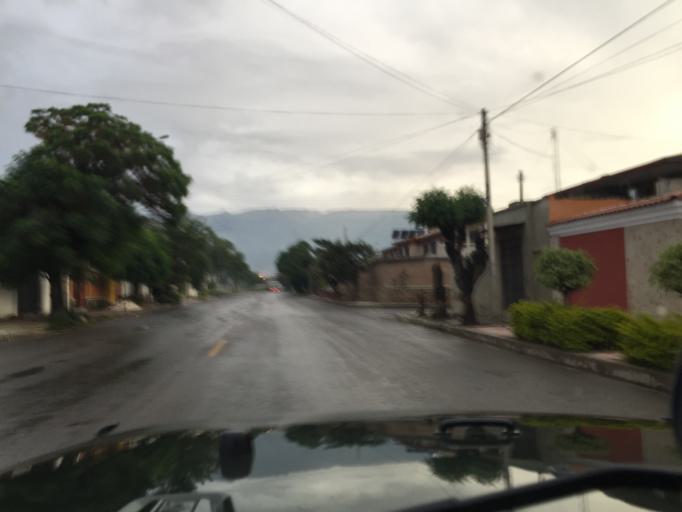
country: BO
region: Cochabamba
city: Cochabamba
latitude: -17.4140
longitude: -66.1688
